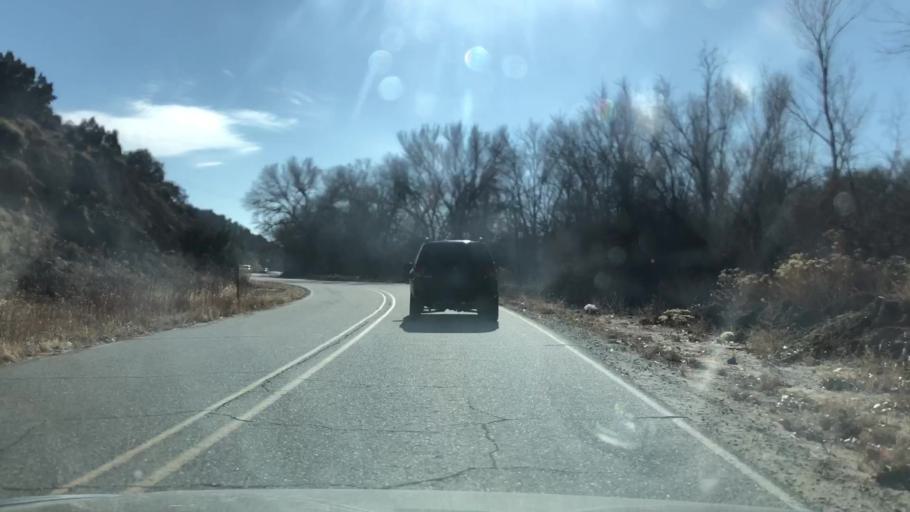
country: US
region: New Mexico
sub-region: Rio Arriba County
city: Ohkay Owingeh
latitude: 36.0891
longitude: -106.1293
